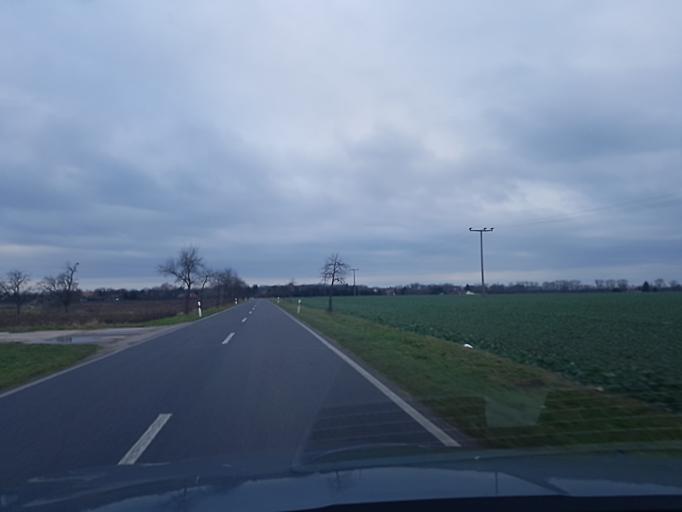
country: DE
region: Brandenburg
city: Sonnewalde
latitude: 51.6940
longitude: 13.6623
